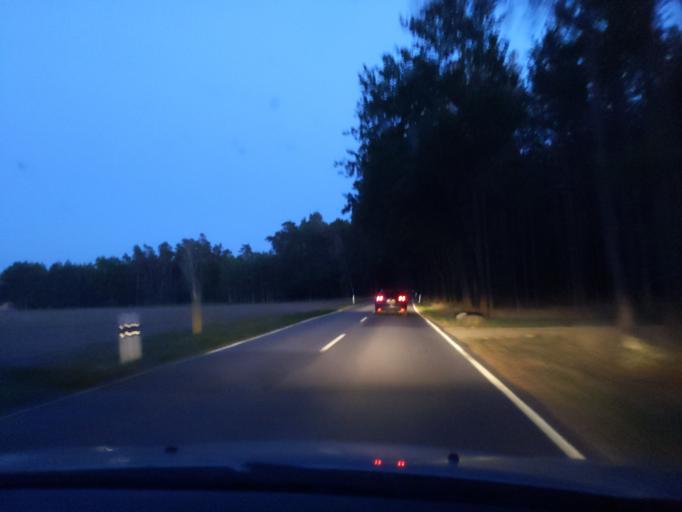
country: DE
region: Saxony
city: Malschwitz
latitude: 51.2789
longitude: 14.5083
